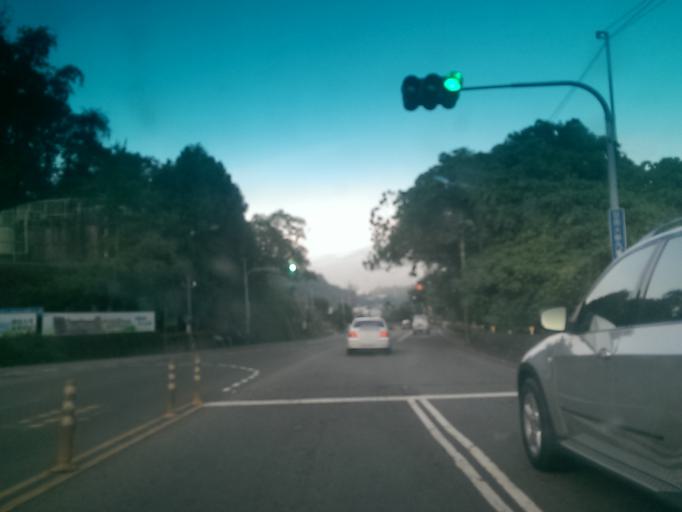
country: TW
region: Taiwan
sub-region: Nantou
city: Puli
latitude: 23.9492
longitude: 120.9378
